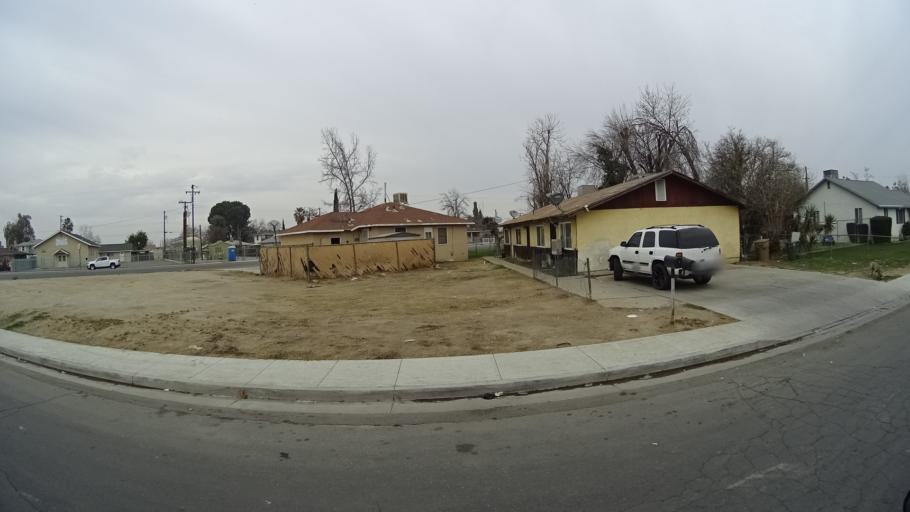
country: US
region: California
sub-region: Kern County
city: Bakersfield
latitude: 35.3491
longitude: -118.9936
